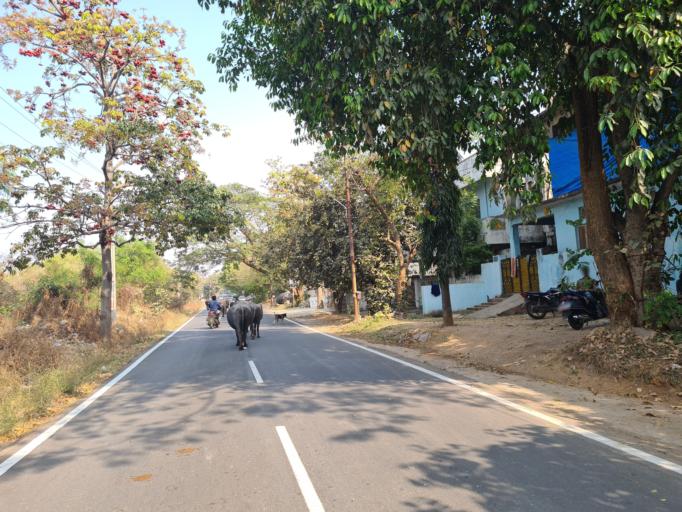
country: IN
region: Telangana
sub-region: Medak
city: Serilingampalle
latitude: 17.4849
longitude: 78.3028
